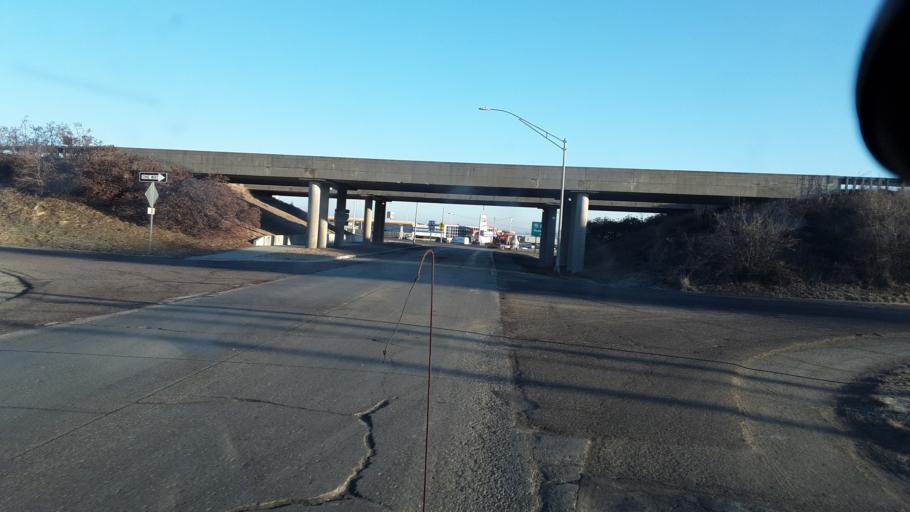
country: US
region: Missouri
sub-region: Lafayette County
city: Concordia
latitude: 38.9913
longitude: -93.5676
